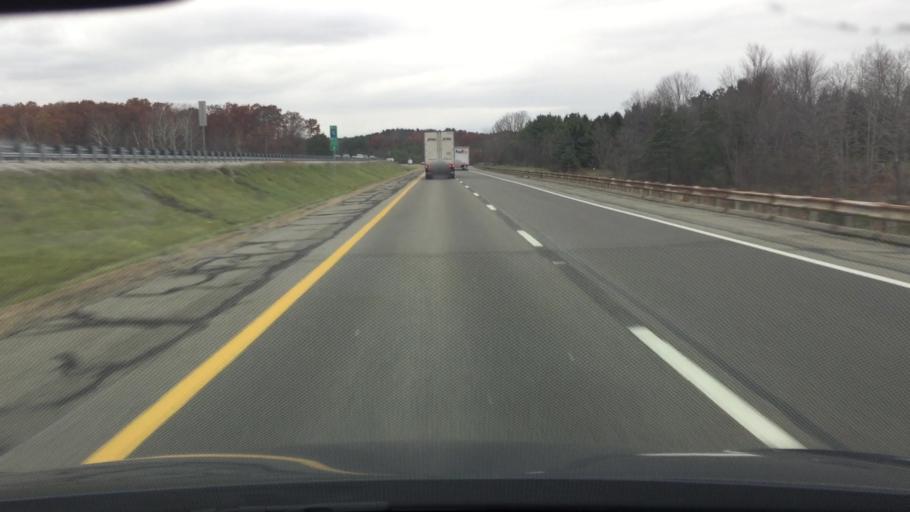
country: US
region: Ohio
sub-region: Mahoning County
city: Austintown
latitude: 41.0735
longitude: -80.7949
